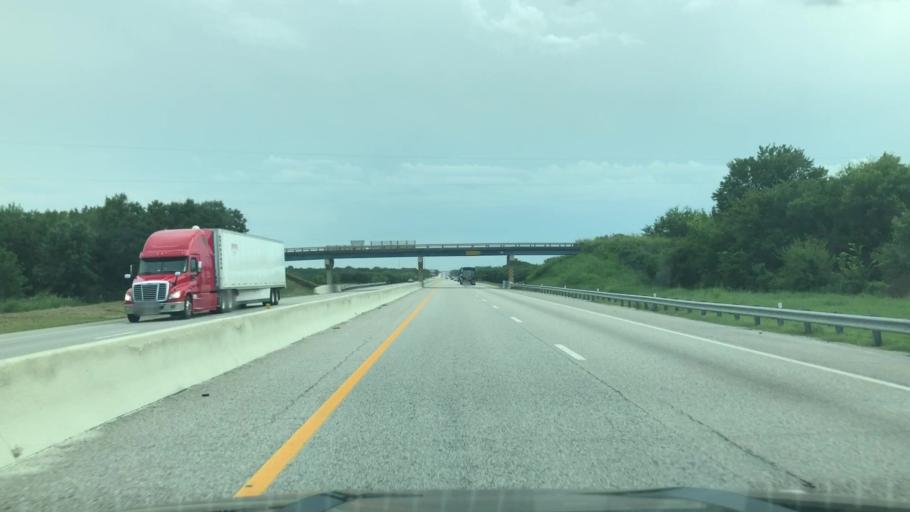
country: US
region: Oklahoma
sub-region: Craig County
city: Vinita
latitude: 36.5988
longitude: -95.1919
